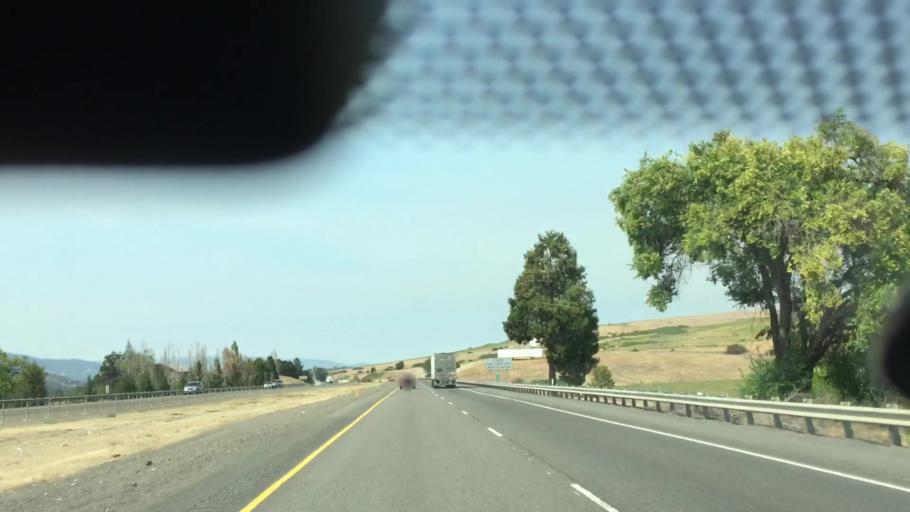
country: US
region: Oregon
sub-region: Jackson County
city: Ashland
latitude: 42.2136
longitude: -122.7040
